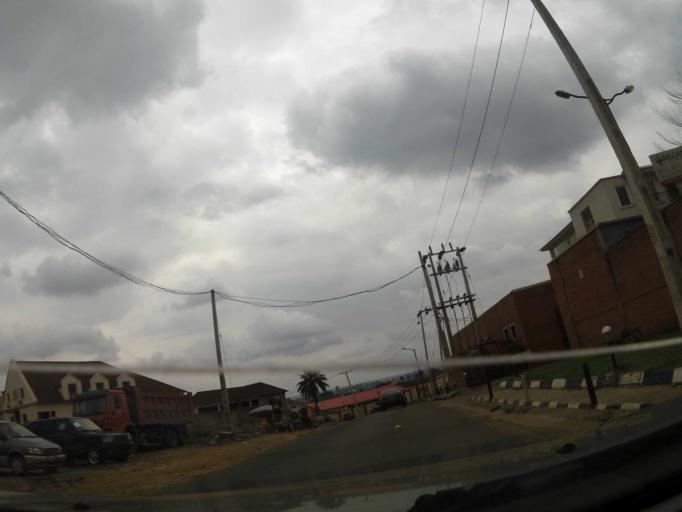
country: NG
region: Oyo
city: Ibadan
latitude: 7.4038
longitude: 3.9249
